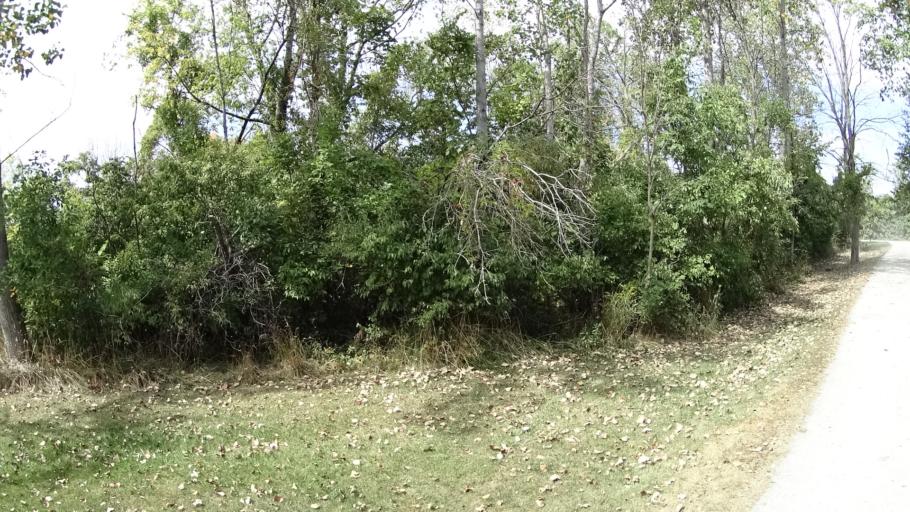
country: US
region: Ohio
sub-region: Erie County
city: Sandusky
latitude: 41.6004
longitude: -82.6821
